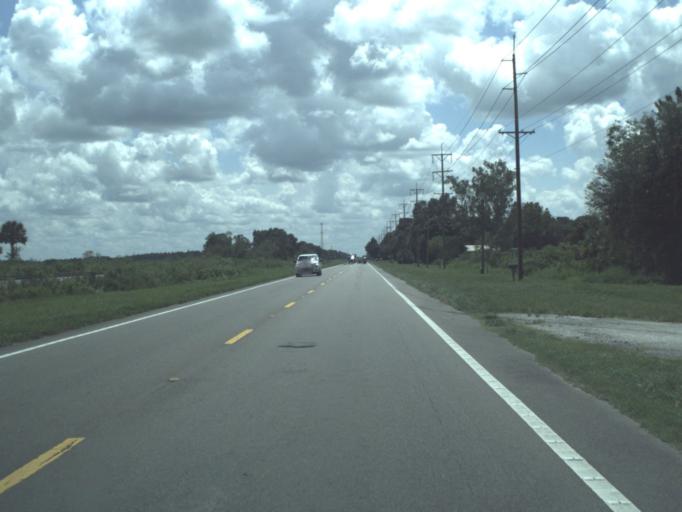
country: US
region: Florida
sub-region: Pasco County
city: Crystal Springs
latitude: 28.1196
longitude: -82.1462
